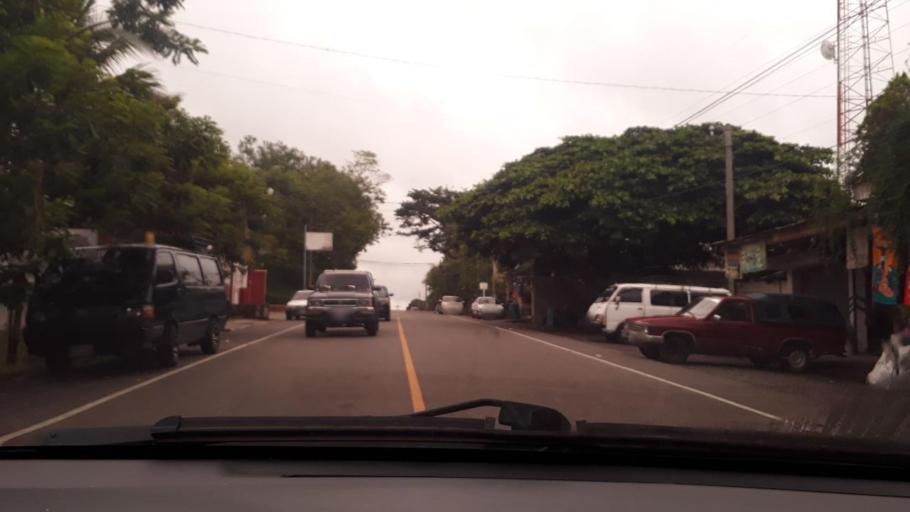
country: GT
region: Chiquimula
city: Esquipulas
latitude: 14.5404
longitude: -89.2838
